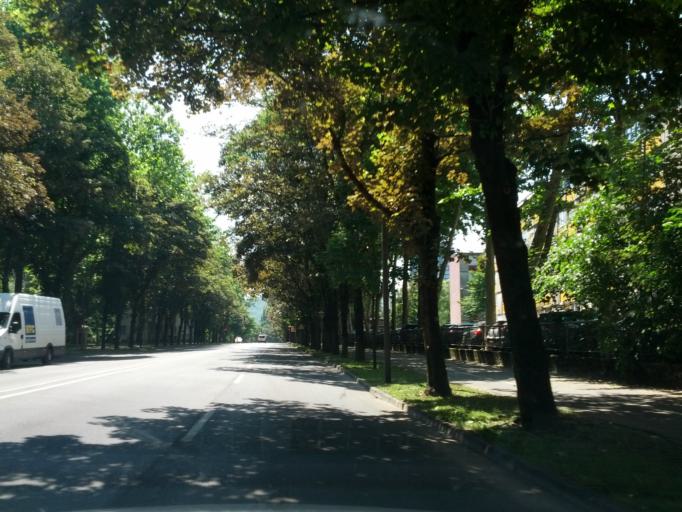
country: SI
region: Ljubljana
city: Ljubljana
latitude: 46.0643
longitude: 14.5185
